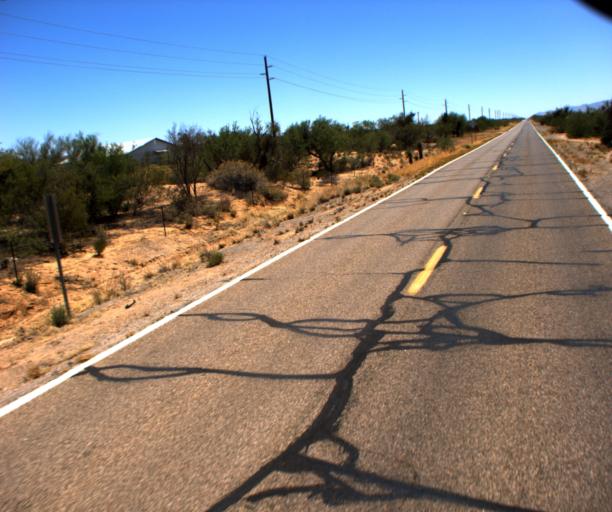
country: US
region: Arizona
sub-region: Pima County
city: Three Points
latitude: 32.0623
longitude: -111.3203
